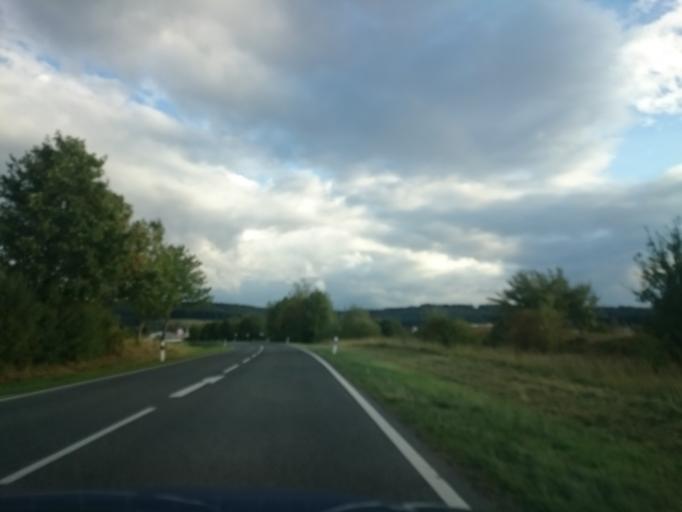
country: DE
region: Bavaria
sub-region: Regierungsbezirk Mittelfranken
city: Thalmassing
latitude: 49.0957
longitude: 11.2099
